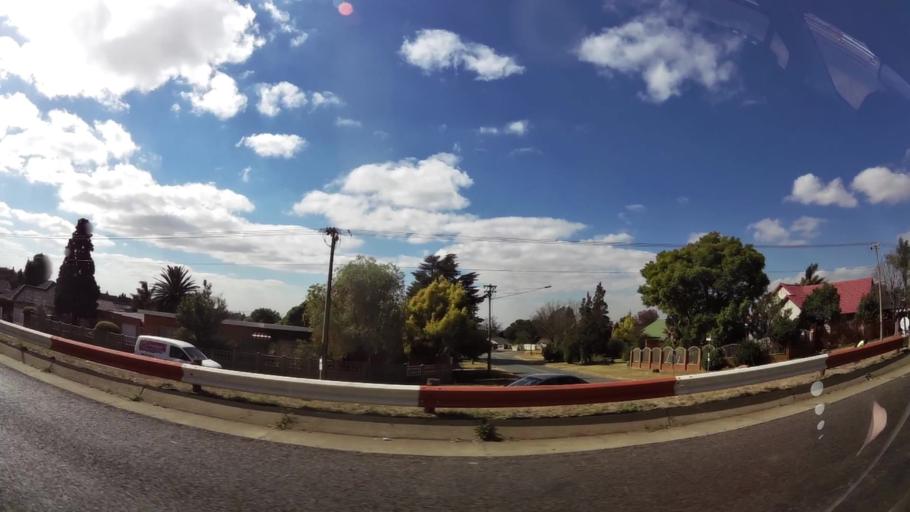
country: ZA
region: Gauteng
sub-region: West Rand District Municipality
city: Krugersdorp
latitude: -26.1172
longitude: 27.8171
